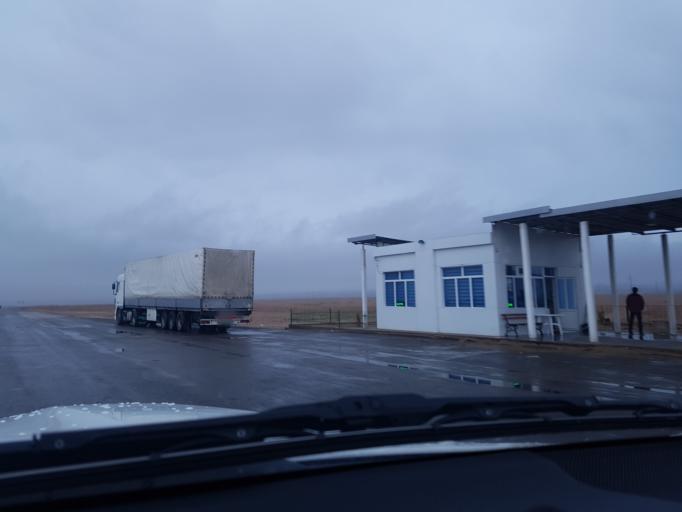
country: TM
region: Balkan
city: Balkanabat
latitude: 39.9425
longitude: 53.8501
